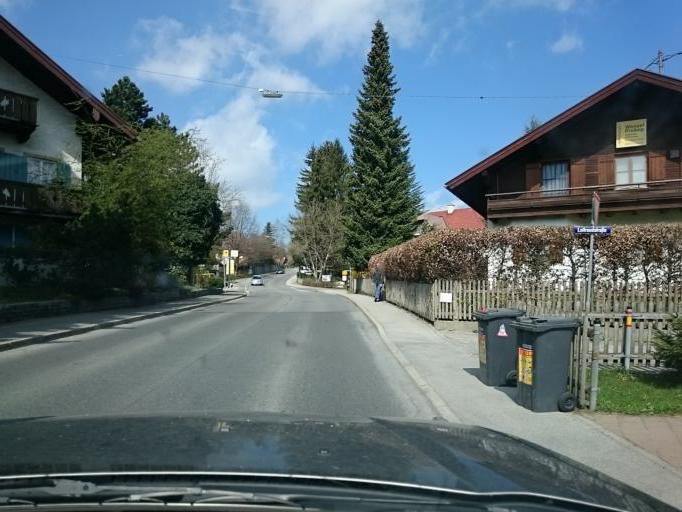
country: DE
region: Bavaria
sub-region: Upper Bavaria
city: Bad Kohlgrub
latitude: 47.6673
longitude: 11.0493
